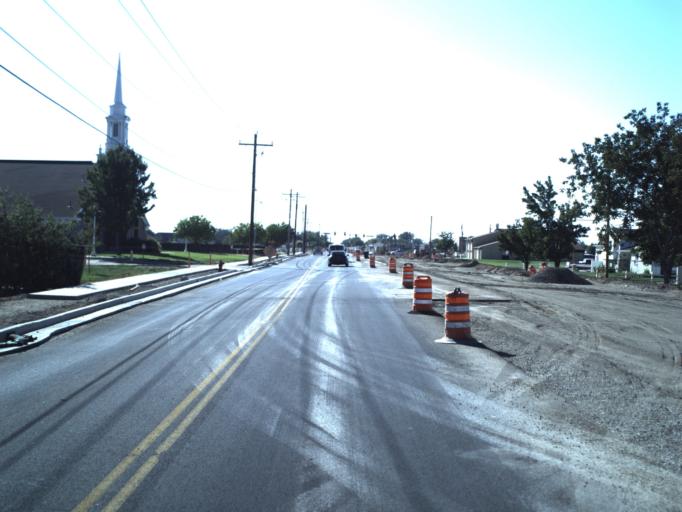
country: US
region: Utah
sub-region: Weber County
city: West Haven
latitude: 41.1907
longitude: -112.0895
